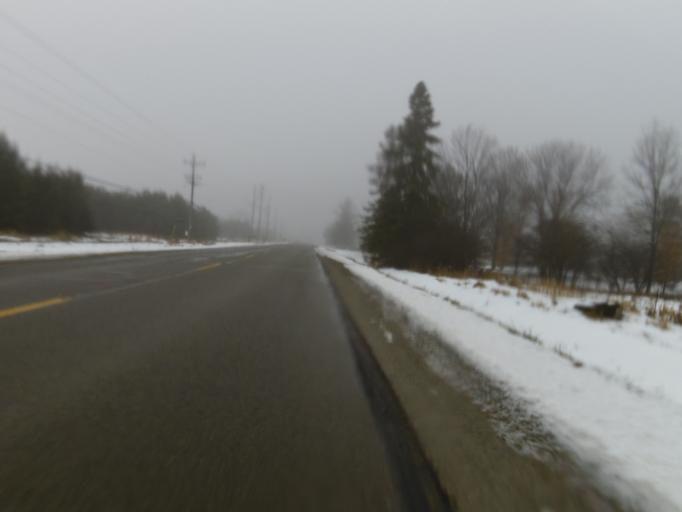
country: CA
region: Ontario
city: Perth
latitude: 44.8707
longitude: -76.3263
